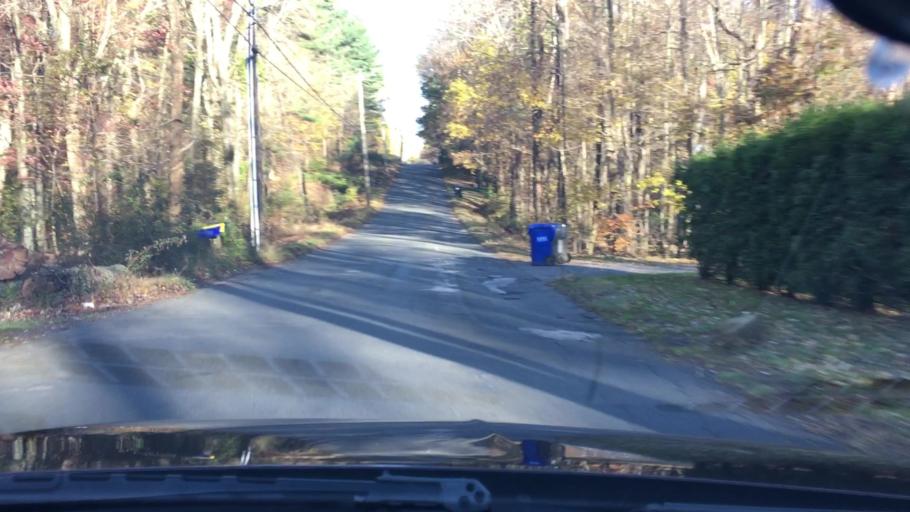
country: US
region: Connecticut
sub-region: Tolland County
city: Crystal Lake
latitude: 41.9541
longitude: -72.4022
